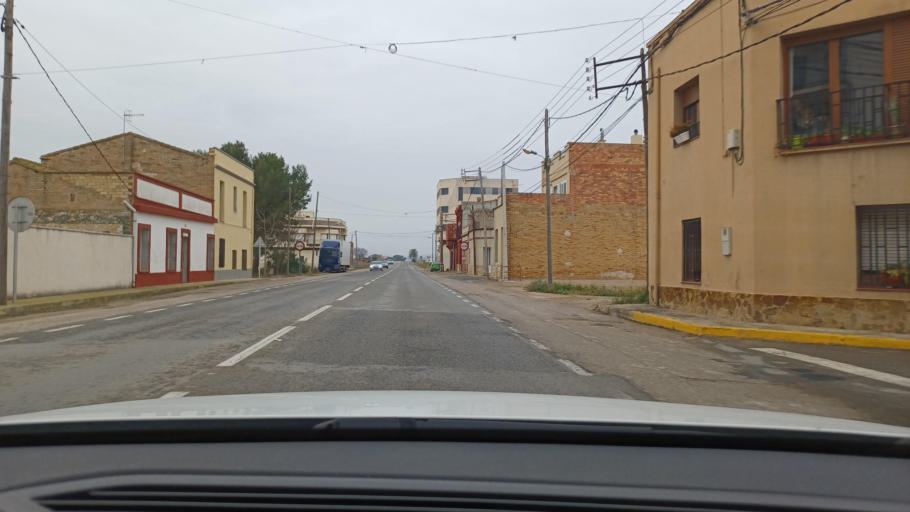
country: ES
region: Catalonia
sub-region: Provincia de Tarragona
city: Amposta
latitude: 40.7402
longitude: 0.6089
